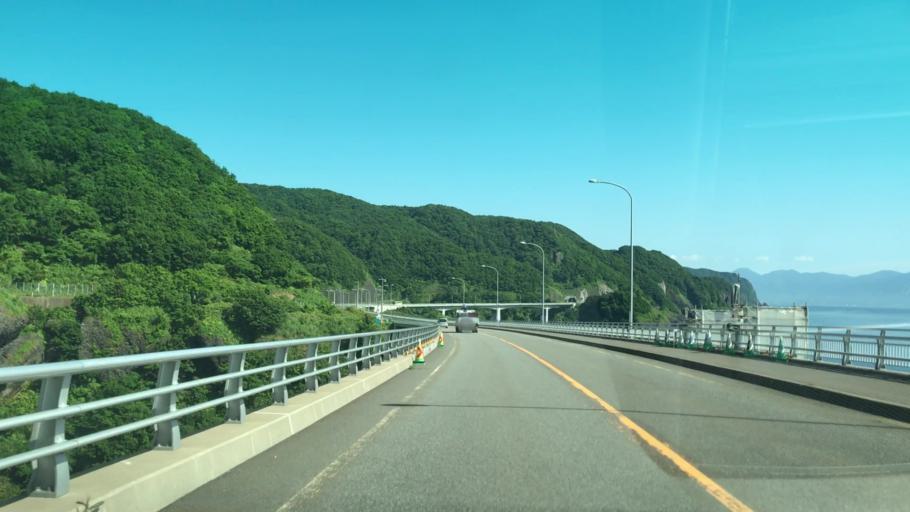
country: JP
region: Hokkaido
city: Iwanai
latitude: 43.1311
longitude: 140.4356
